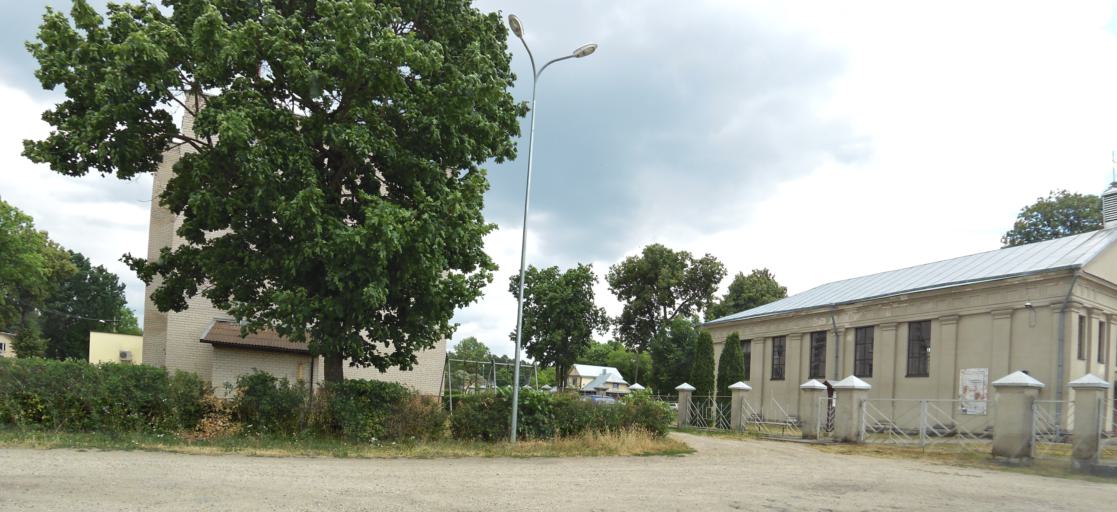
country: LT
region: Vilnius County
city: Ukmerge
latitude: 55.2141
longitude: 24.7877
